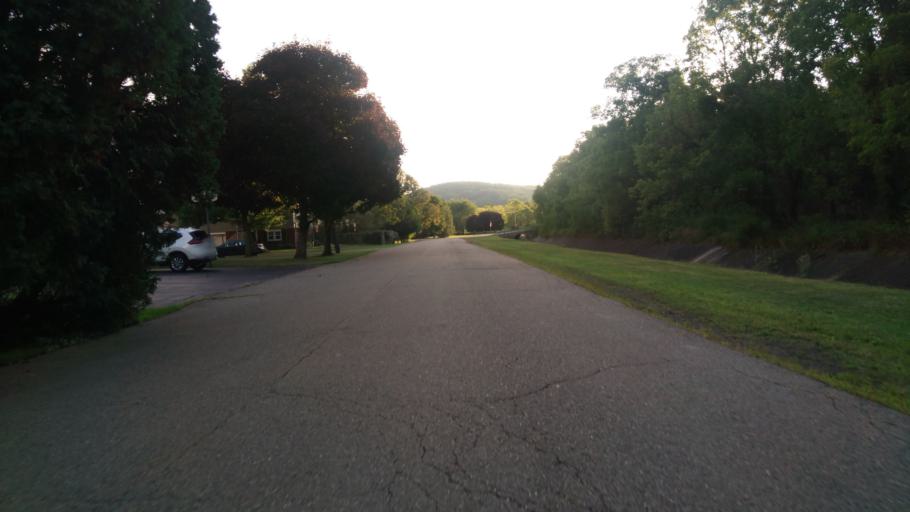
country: US
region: New York
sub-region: Chemung County
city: Southport
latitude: 42.0578
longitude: -76.8306
